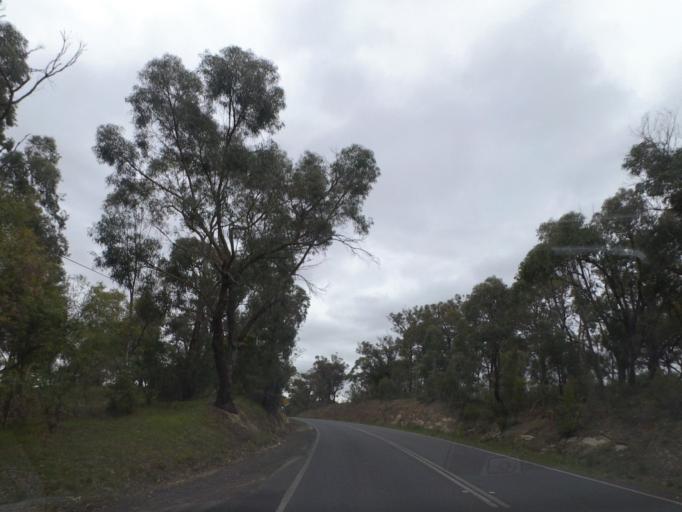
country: AU
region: Victoria
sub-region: Nillumbik
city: Diamond Creek
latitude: -37.6494
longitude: 145.1474
